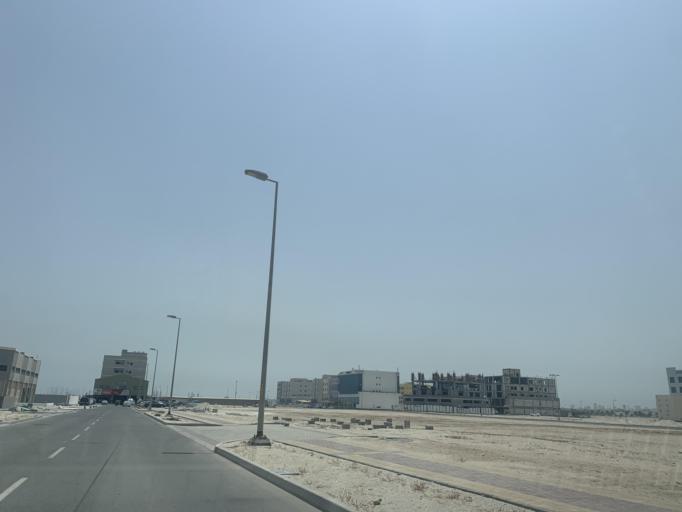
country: BH
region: Muharraq
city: Al Hadd
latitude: 26.2583
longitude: 50.6671
